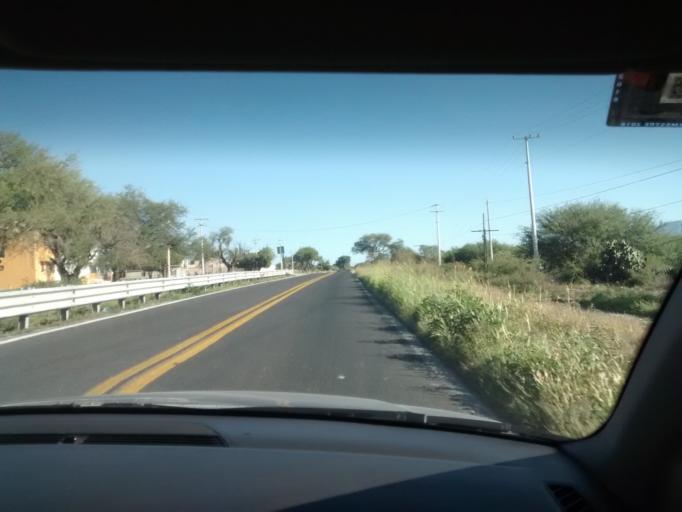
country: MX
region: Puebla
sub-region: Tepanco de Lopez
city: San Andres Cacaloapan
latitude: 18.5745
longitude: -97.5771
